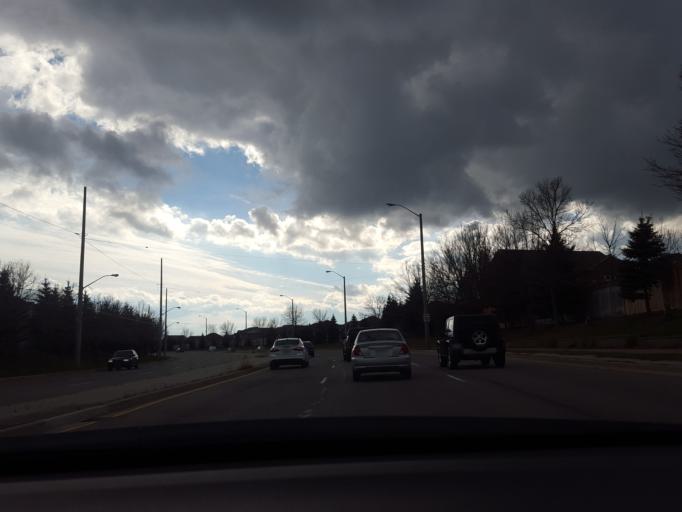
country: CA
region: Ontario
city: Brampton
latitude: 43.6277
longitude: -79.7423
